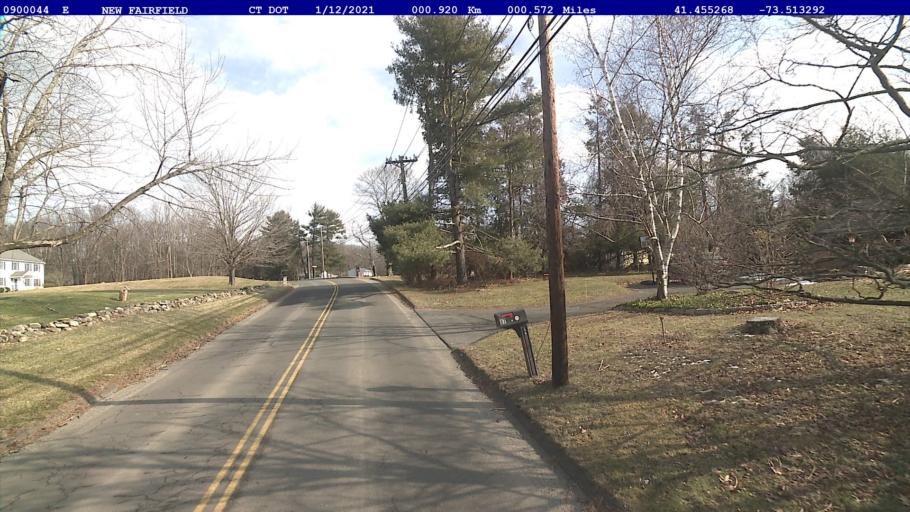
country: US
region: New York
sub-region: Putnam County
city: Putnam Lake
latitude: 41.4553
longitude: -73.5133
